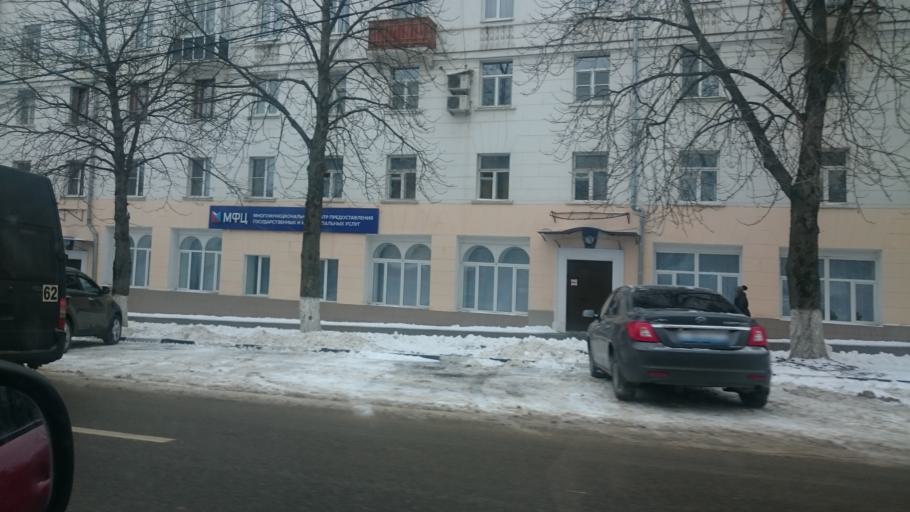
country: RU
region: Tula
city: Tula
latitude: 54.1819
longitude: 37.6053
